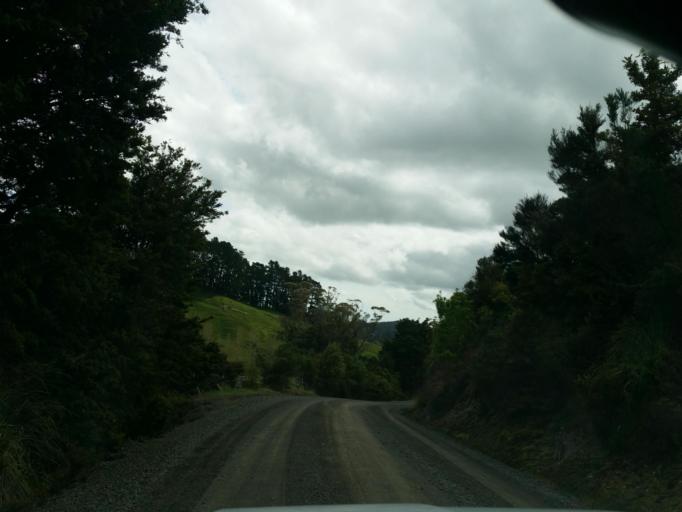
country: NZ
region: Northland
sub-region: Kaipara District
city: Dargaville
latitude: -35.8995
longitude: 174.0133
